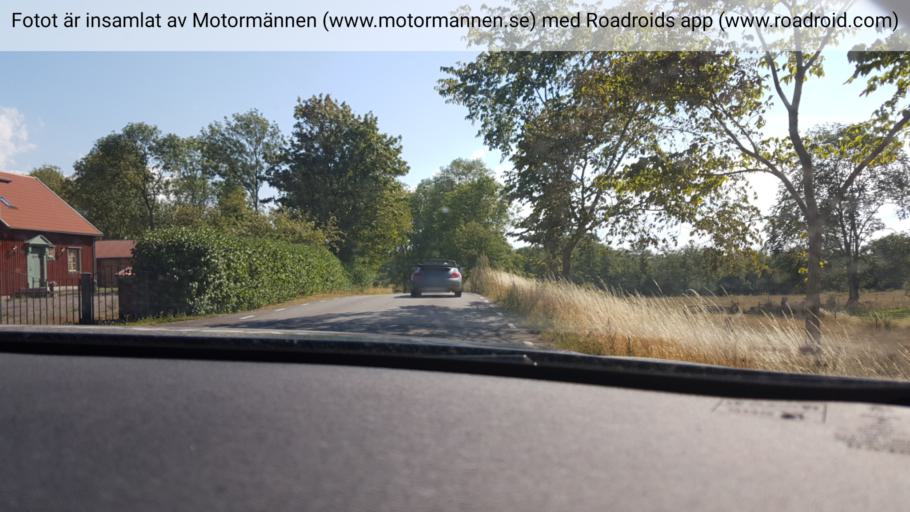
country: SE
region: Vaestra Goetaland
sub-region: Gotene Kommun
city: Kallby
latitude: 58.5453
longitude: 13.3307
